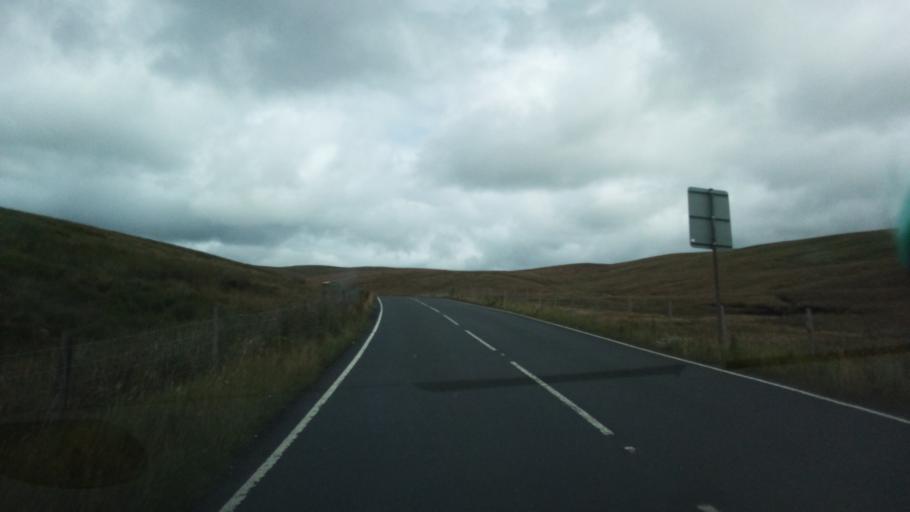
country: GB
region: England
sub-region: North Yorkshire
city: Settle
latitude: 54.2346
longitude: -2.3159
